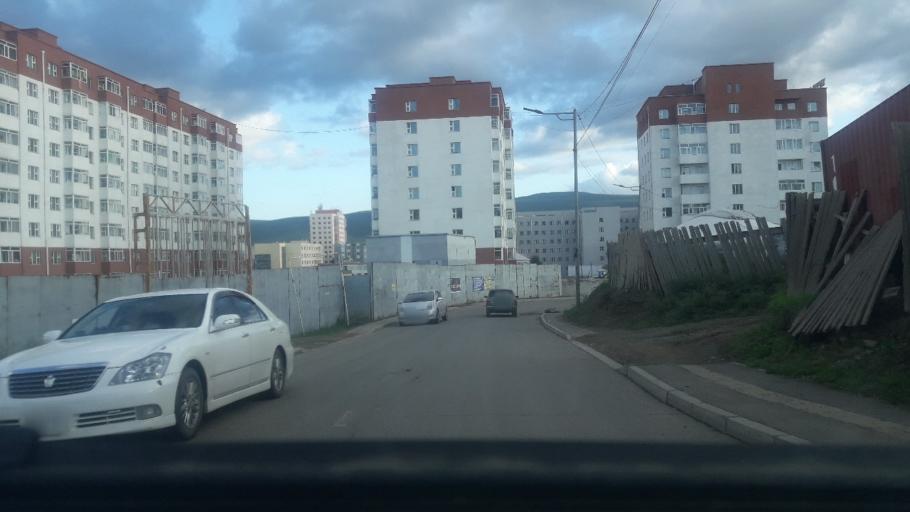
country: MN
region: Ulaanbaatar
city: Ulaanbaatar
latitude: 47.9182
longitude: 106.9955
